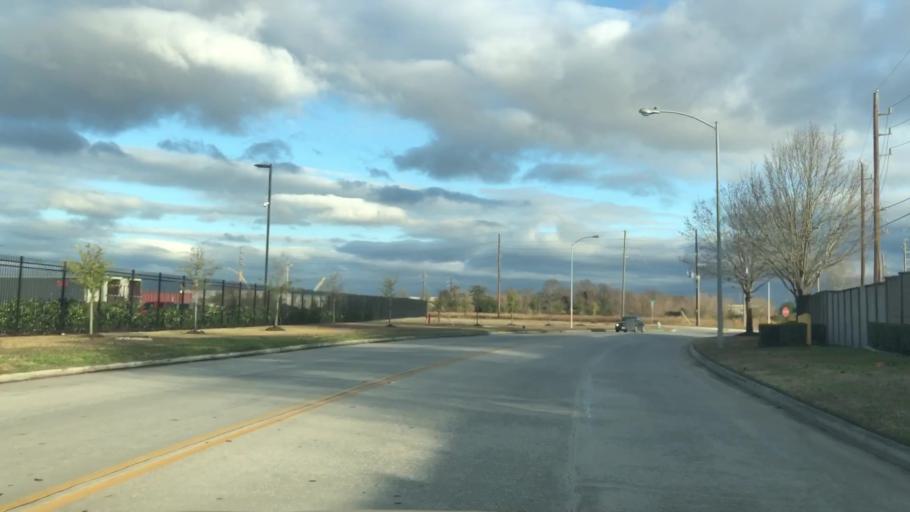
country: US
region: Texas
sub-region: Harris County
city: Aldine
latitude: 29.9169
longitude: -95.4166
